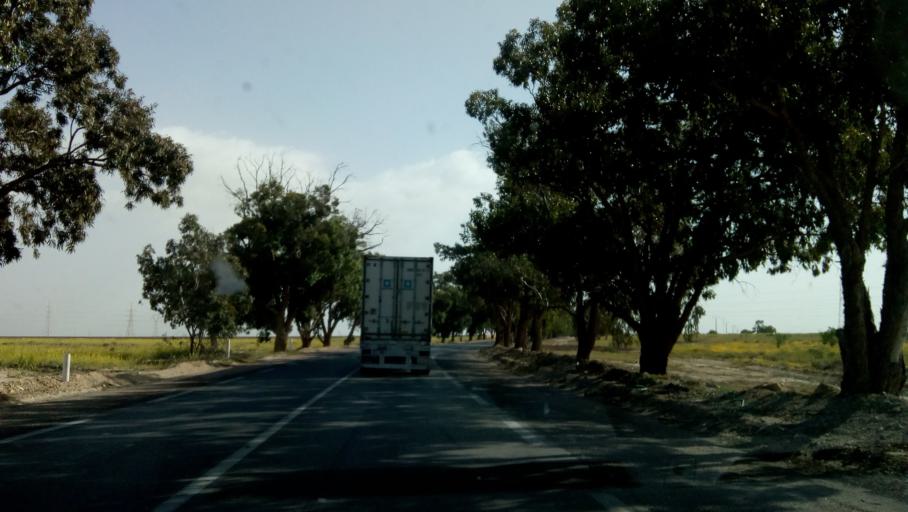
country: TN
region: Qabis
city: Gabes
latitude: 33.8908
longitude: 10.0299
